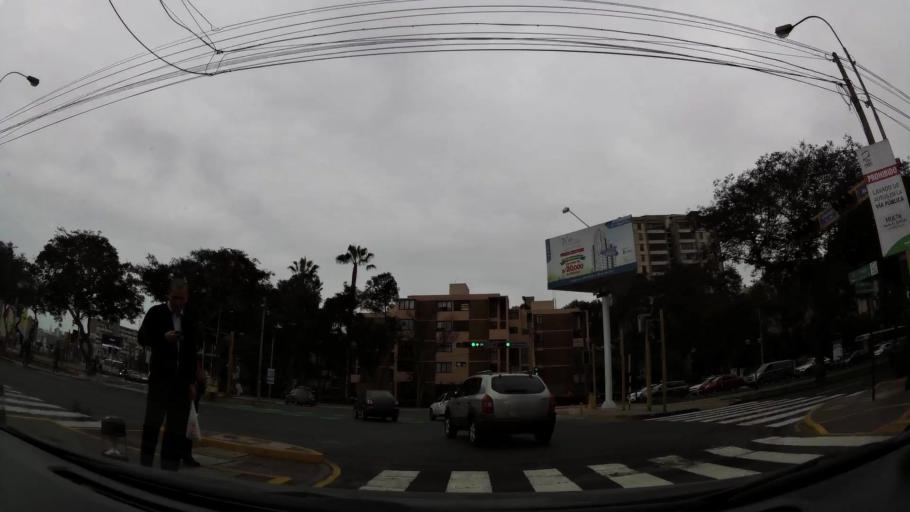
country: PE
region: Lima
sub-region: Lima
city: San Isidro
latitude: -12.0880
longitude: -77.0505
